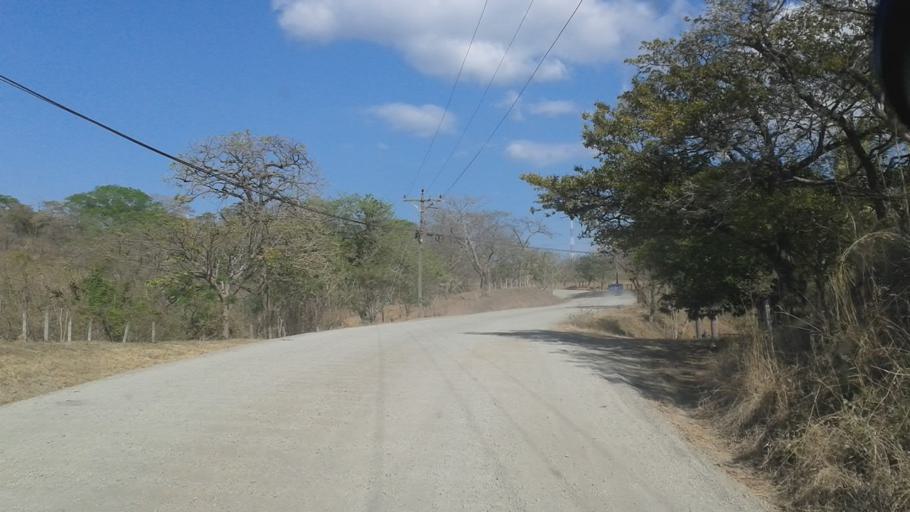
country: CR
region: Guanacaste
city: Santa Cruz
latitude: 10.1143
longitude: -85.7819
